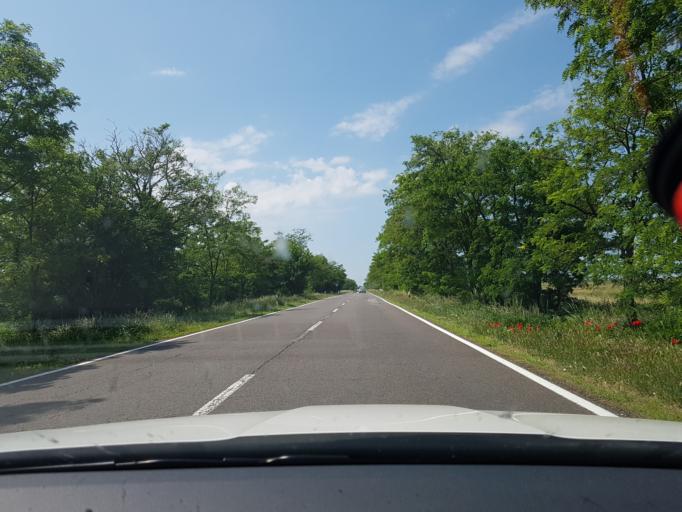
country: HU
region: Hajdu-Bihar
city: Egyek
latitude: 47.5488
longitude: 20.9341
